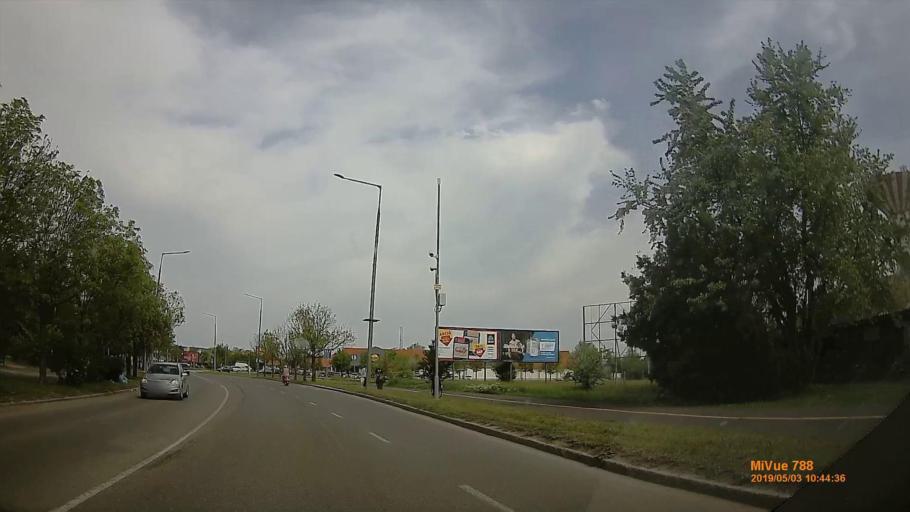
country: HU
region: Jasz-Nagykun-Szolnok
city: Szolnok
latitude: 47.1898
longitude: 20.1944
